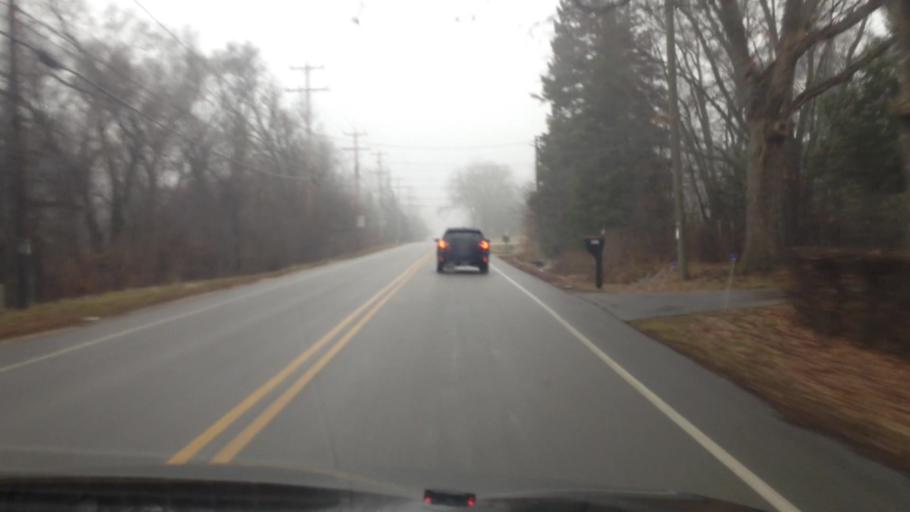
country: US
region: Wisconsin
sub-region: Milwaukee County
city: Hales Corners
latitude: 42.9247
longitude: -88.0554
